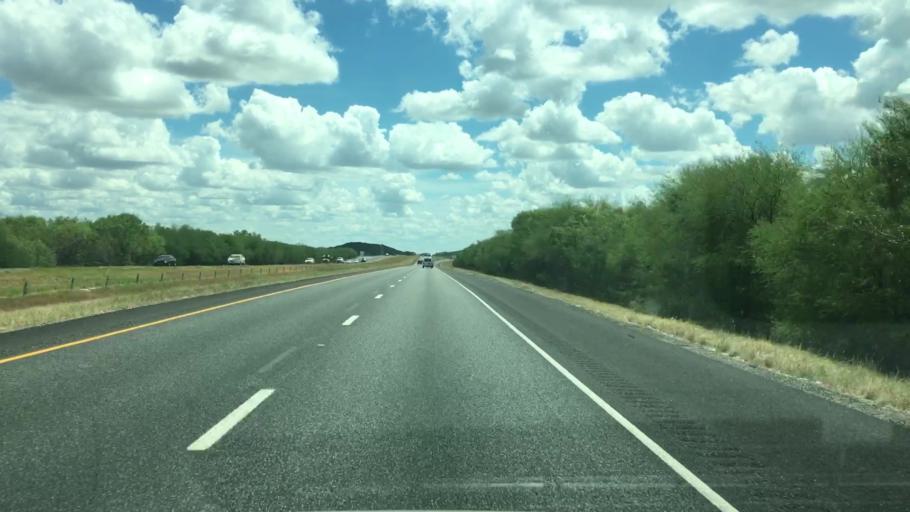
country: US
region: Texas
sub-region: Atascosa County
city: Pleasanton
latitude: 28.7418
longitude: -98.2922
